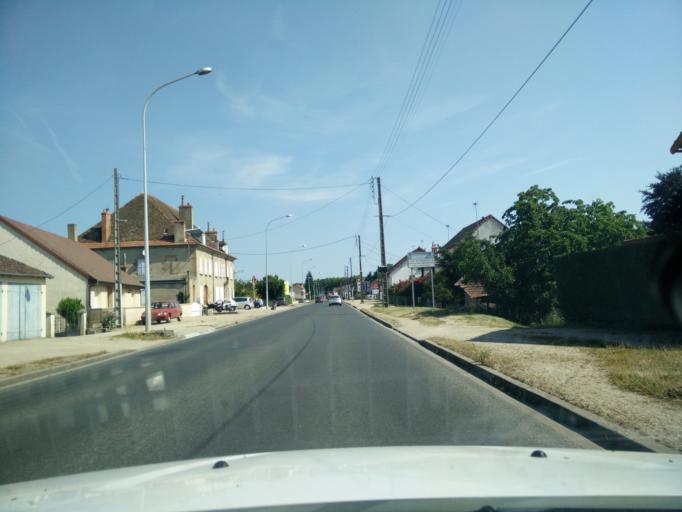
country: FR
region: Auvergne
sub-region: Departement de l'Allier
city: Moulins
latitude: 46.5554
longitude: 3.3211
